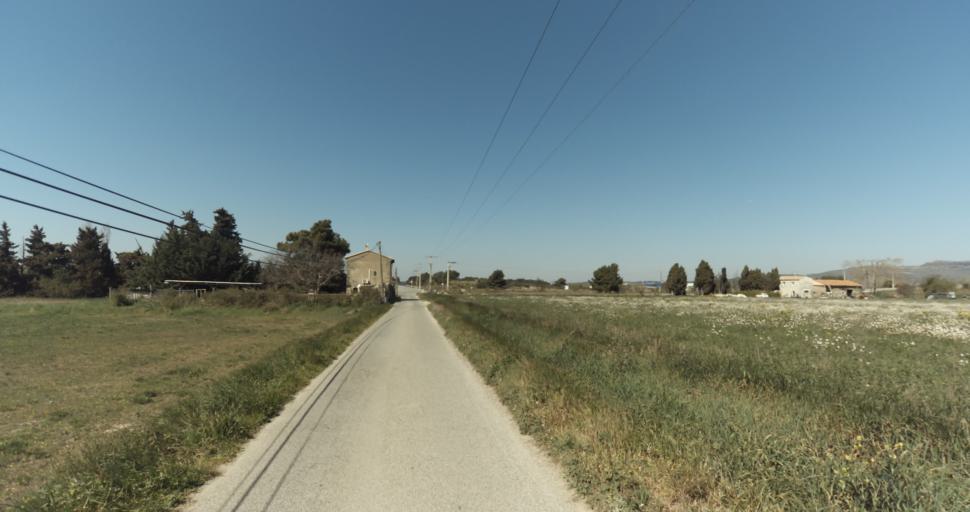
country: FR
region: Provence-Alpes-Cote d'Azur
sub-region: Departement des Bouches-du-Rhone
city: Lancon-Provence
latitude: 43.6131
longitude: 5.1402
